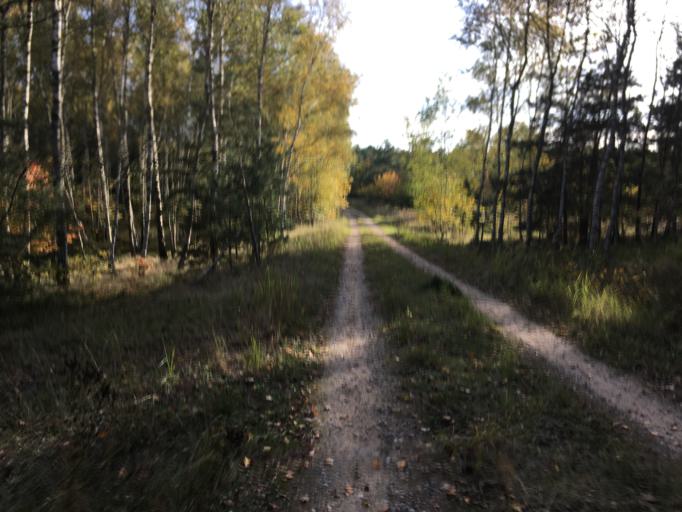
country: DE
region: Brandenburg
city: Birkenwerder
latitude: 52.6978
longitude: 13.3427
